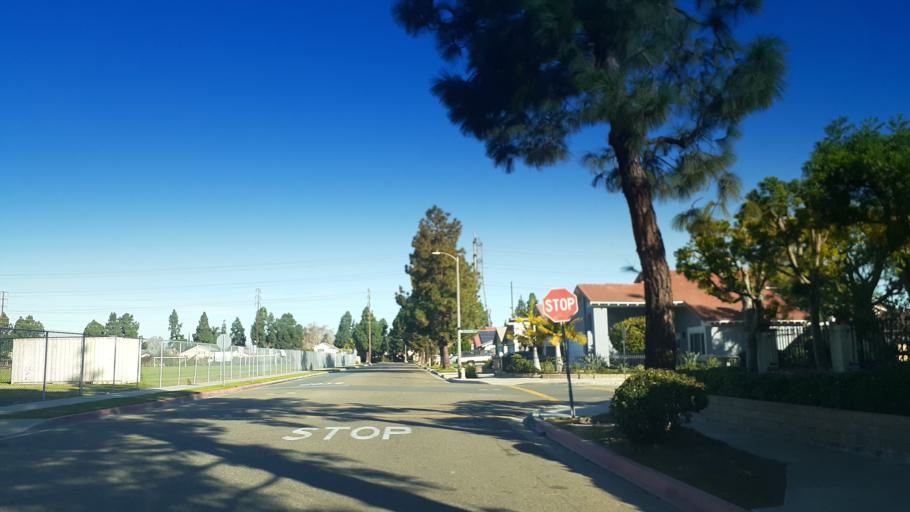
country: US
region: California
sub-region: Los Angeles County
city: Cerritos
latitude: 33.8480
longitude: -118.0678
